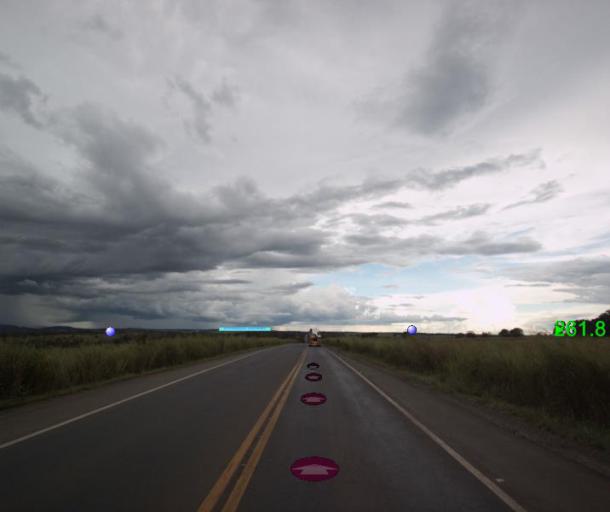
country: BR
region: Goias
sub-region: Itapaci
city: Itapaci
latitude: -15.0113
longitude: -49.4185
